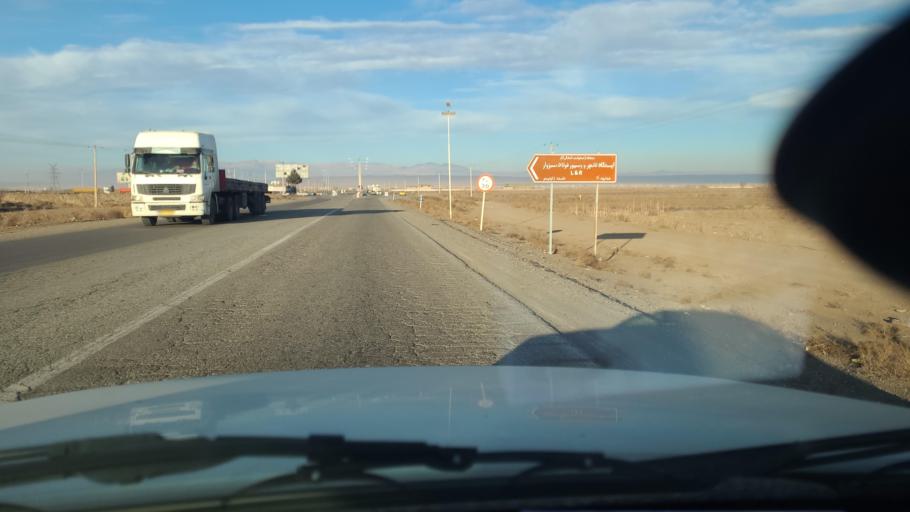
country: IR
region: Razavi Khorasan
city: Neqab
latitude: 36.5827
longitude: 57.5804
